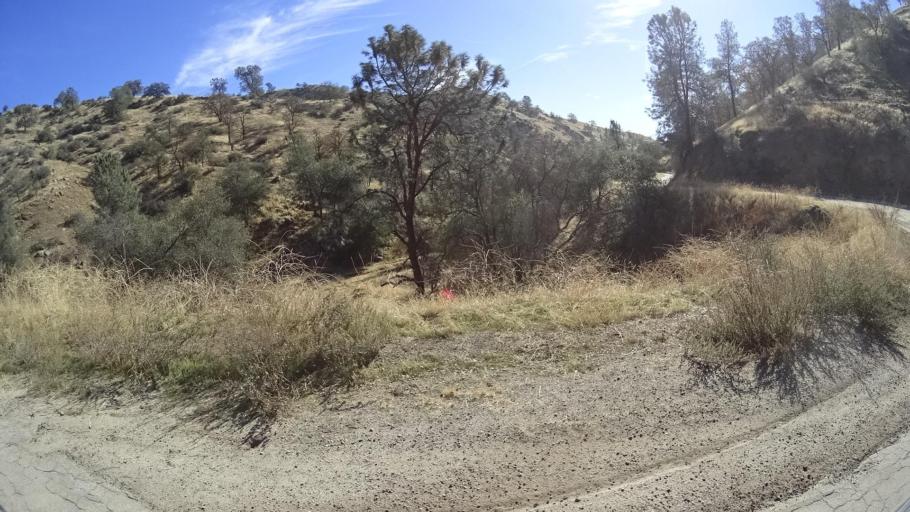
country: US
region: California
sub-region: Kern County
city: Arvin
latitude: 35.4325
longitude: -118.7290
